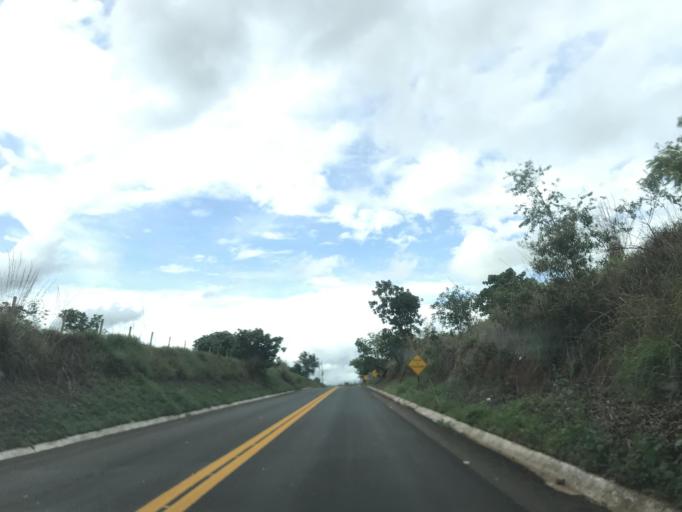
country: BR
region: Goias
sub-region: Bela Vista De Goias
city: Bela Vista de Goias
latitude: -17.0619
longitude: -48.6576
